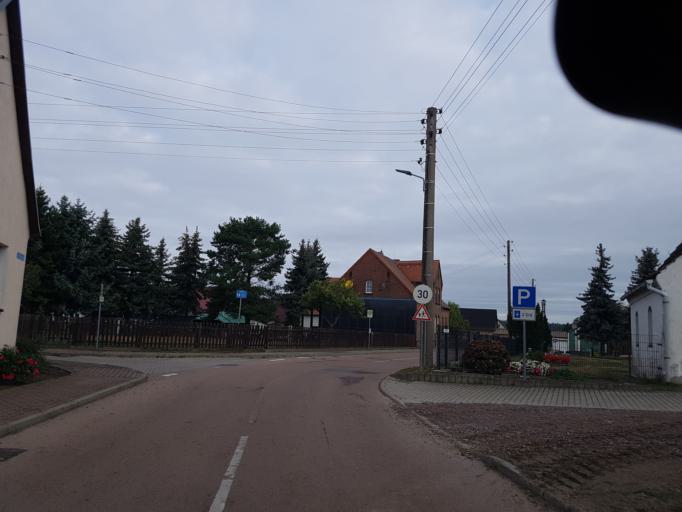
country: DE
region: Saxony-Anhalt
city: Rosslau
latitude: 51.9800
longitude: 12.2971
